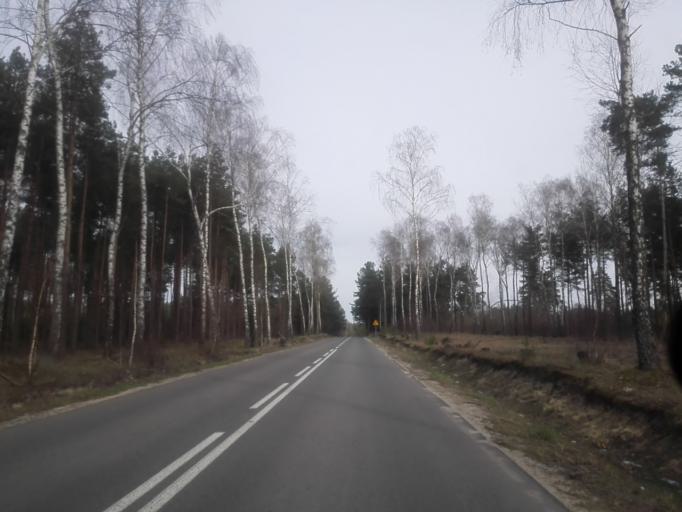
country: PL
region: Silesian Voivodeship
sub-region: Powiat myszkowski
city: Choron
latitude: 50.7076
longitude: 19.3418
